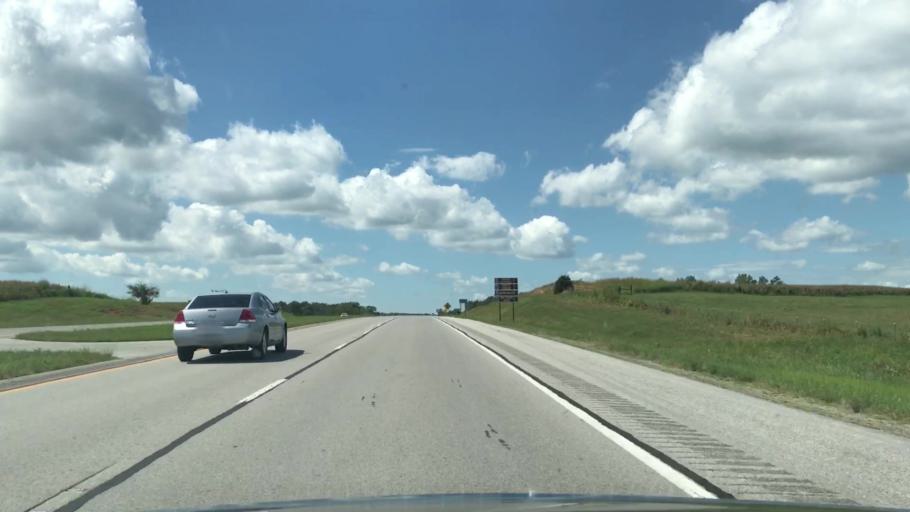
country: US
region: Kentucky
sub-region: Logan County
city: Auburn
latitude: 36.8880
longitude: -86.6580
